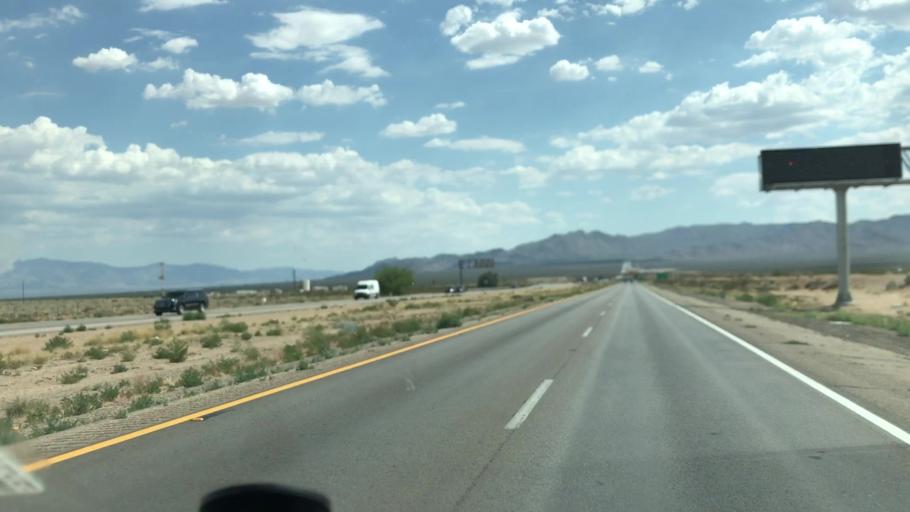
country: US
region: Nevada
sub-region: Clark County
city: Sandy Valley
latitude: 35.5487
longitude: -115.4166
